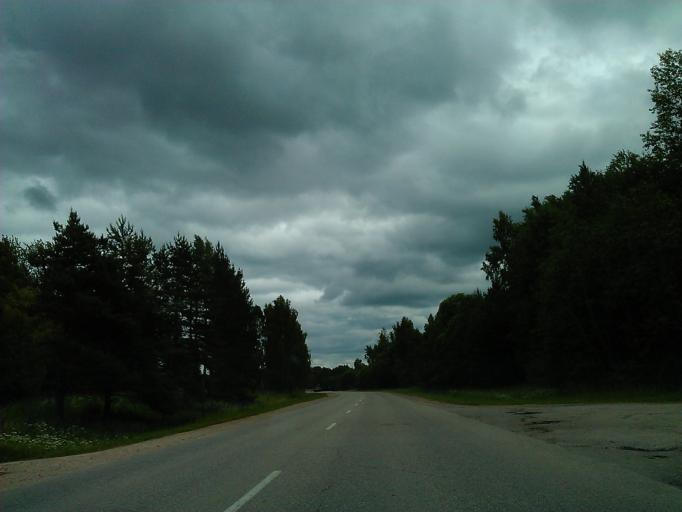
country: LV
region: Kuldigas Rajons
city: Kuldiga
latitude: 56.9627
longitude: 21.9391
